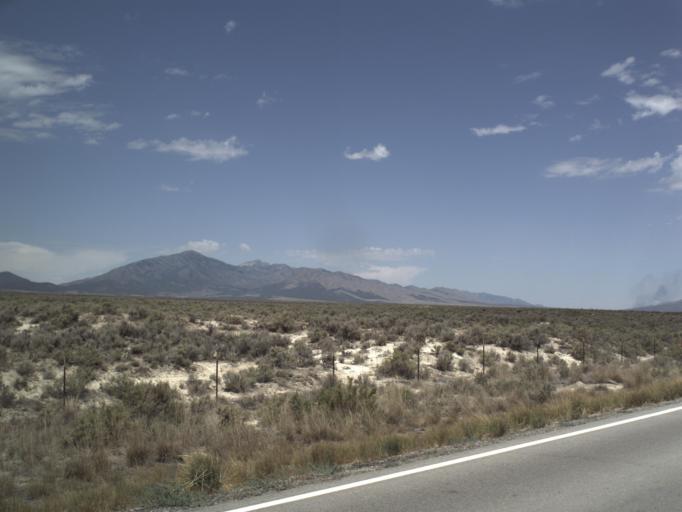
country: US
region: Utah
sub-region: Tooele County
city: Tooele
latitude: 40.2166
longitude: -112.4061
